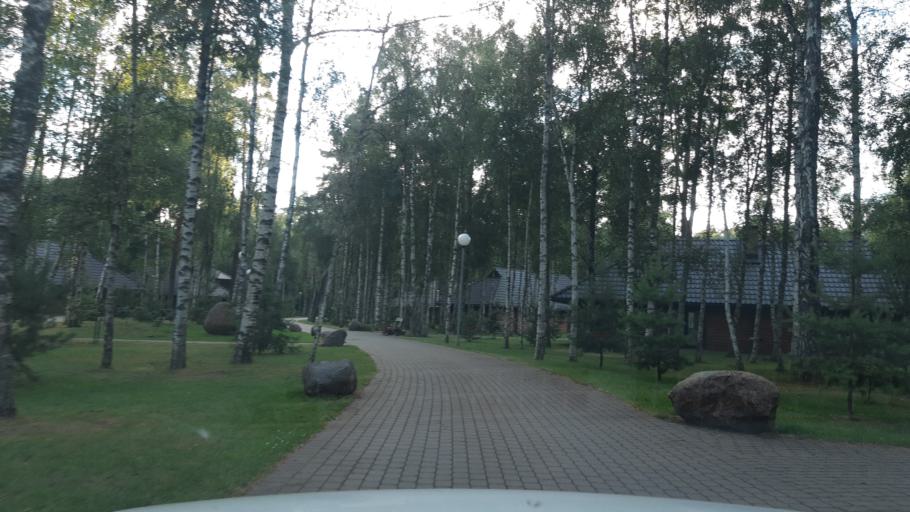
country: LT
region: Klaipedos apskritis
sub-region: Klaipeda
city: Palanga
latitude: 55.9591
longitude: 21.1247
